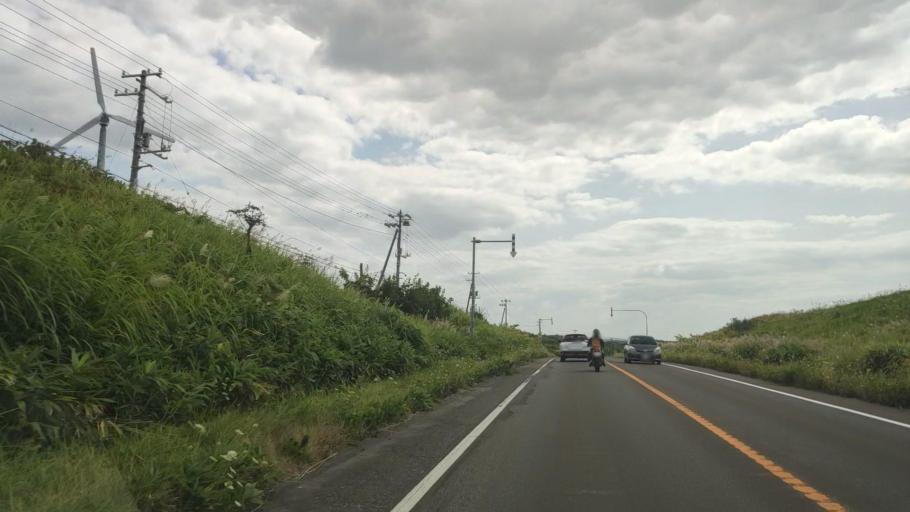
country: JP
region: Hokkaido
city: Rumoi
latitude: 44.5152
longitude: 141.7663
